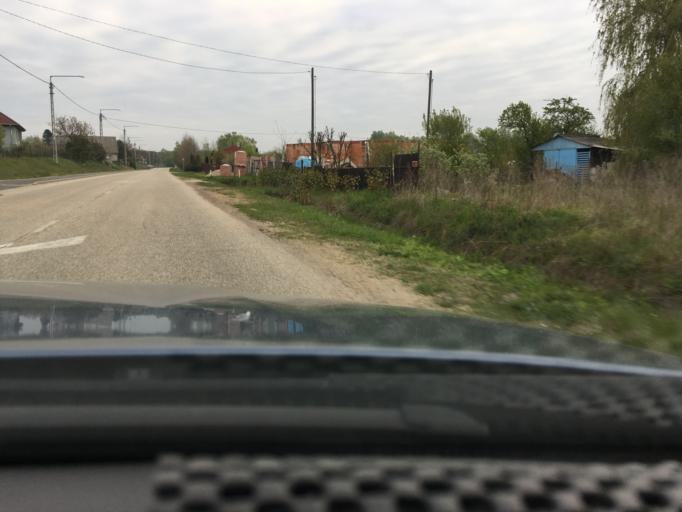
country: HU
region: Hajdu-Bihar
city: Hajdusamson
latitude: 47.5692
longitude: 21.7694
